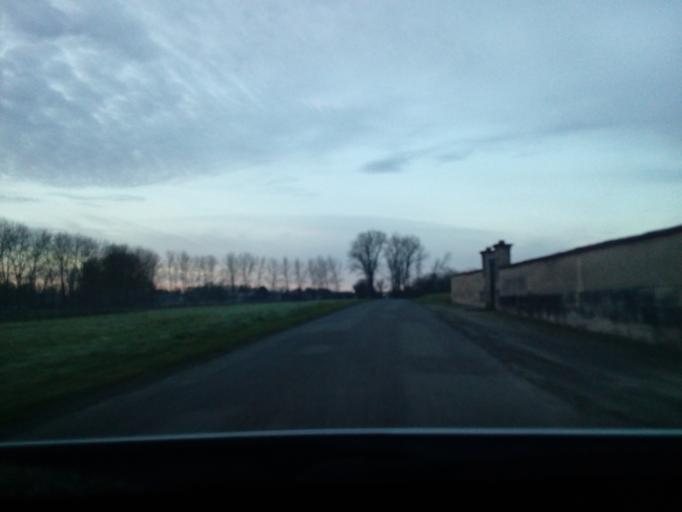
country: FR
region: Poitou-Charentes
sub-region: Departement de la Charente-Maritime
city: Perignac
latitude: 45.6134
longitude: -0.4207
